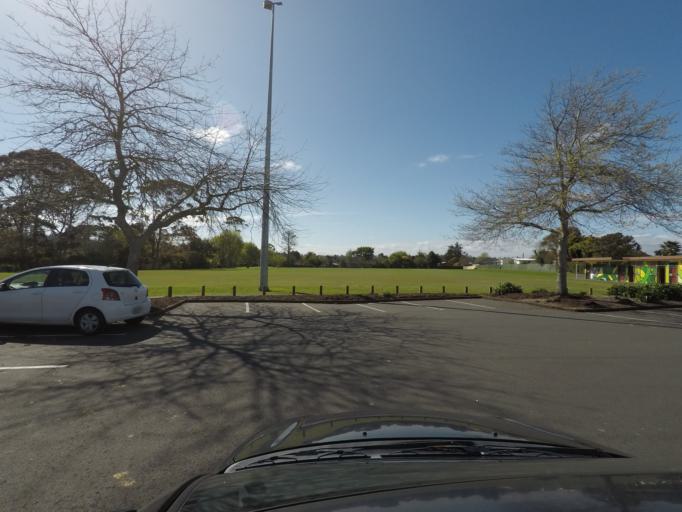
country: NZ
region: Auckland
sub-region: Auckland
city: Rosebank
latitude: -36.8666
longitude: 174.6002
